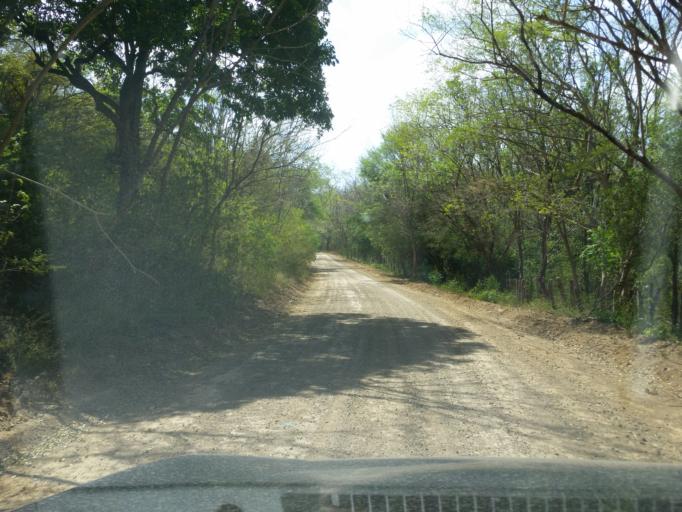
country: NI
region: Rivas
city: San Juan del Sur
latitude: 11.1327
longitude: -85.7808
